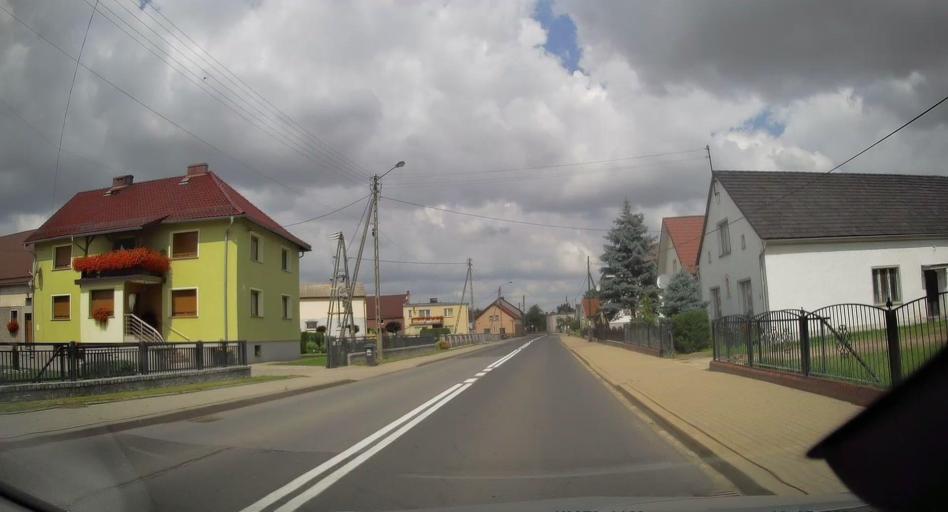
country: PL
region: Opole Voivodeship
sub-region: Powiat prudnicki
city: Twardawa
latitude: 50.3351
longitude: 17.9690
